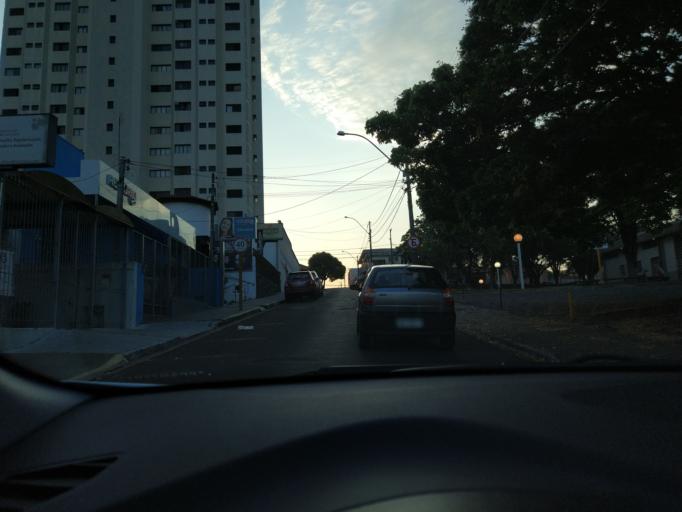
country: BR
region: Sao Paulo
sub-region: Botucatu
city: Botucatu
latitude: -22.8920
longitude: -48.4421
